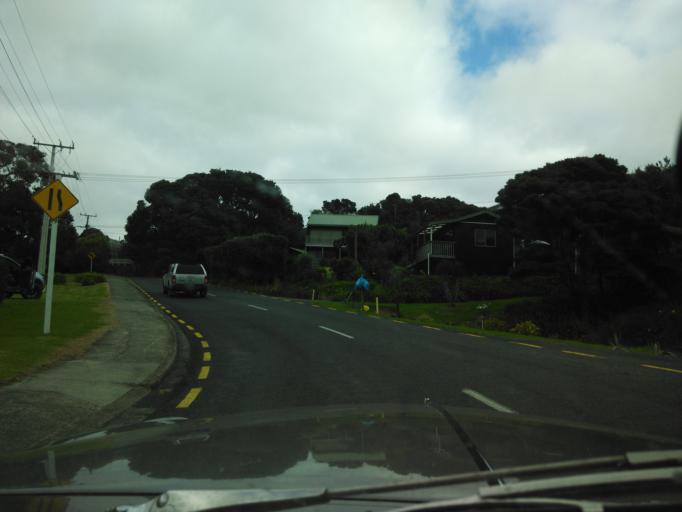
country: NZ
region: Auckland
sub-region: Auckland
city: Wellsford
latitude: -36.0832
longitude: 174.5885
